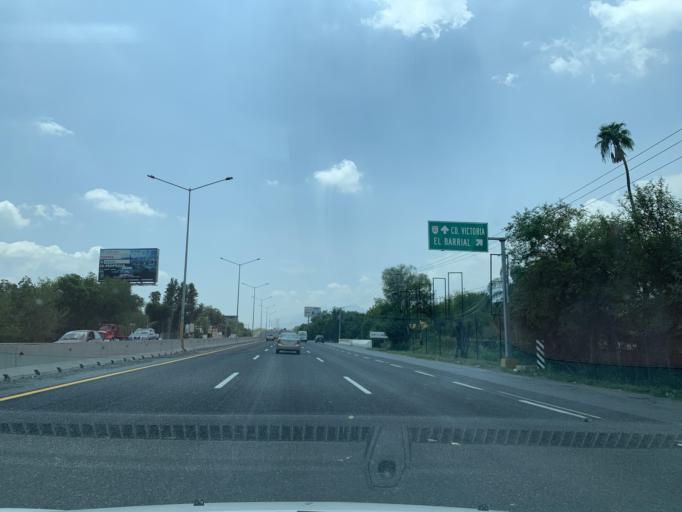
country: MX
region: Nuevo Leon
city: Santiago
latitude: 25.4836
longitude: -100.1815
